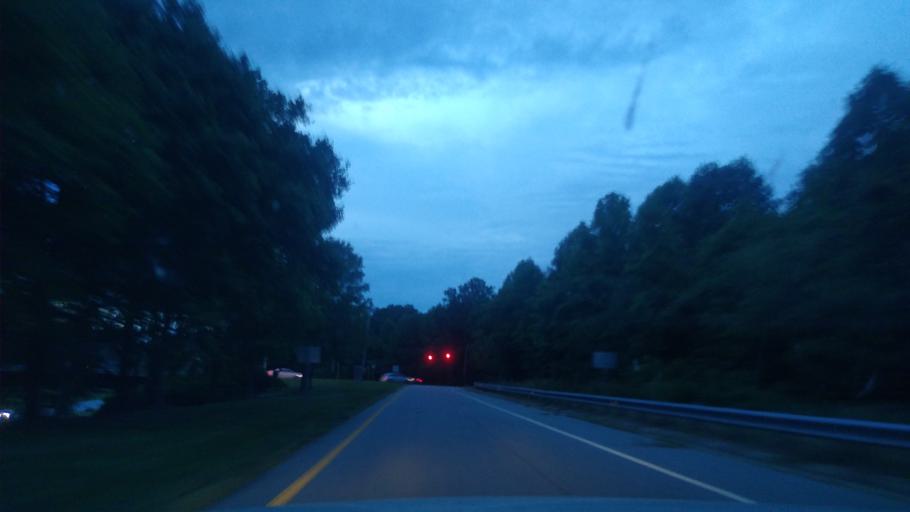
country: US
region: North Carolina
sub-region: Guilford County
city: Greensboro
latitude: 36.1035
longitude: -79.8373
